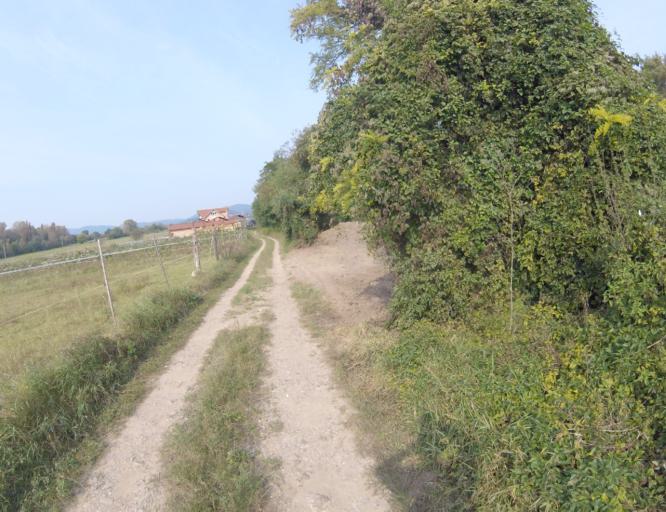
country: HU
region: Pest
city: Veroce
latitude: 47.8183
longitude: 19.0658
